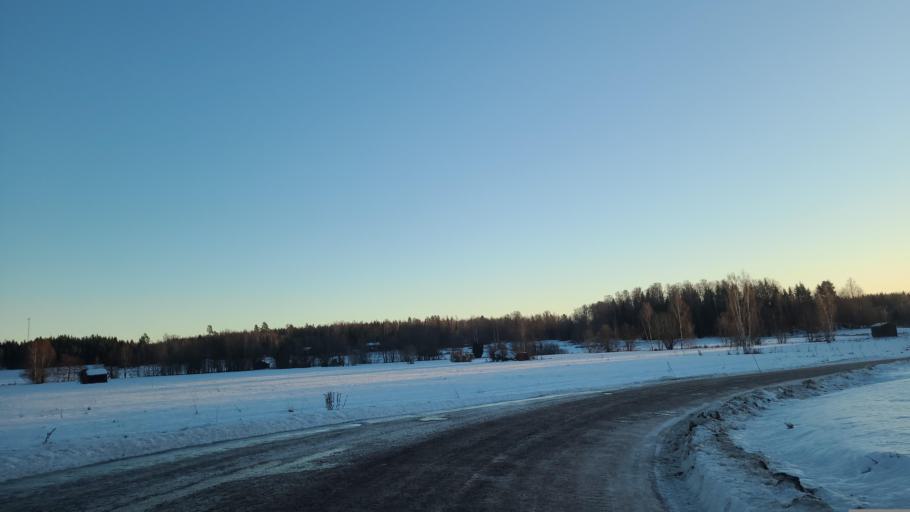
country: SE
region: Gaevleborg
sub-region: Soderhamns Kommun
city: Soderhamn
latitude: 61.2719
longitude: 16.9964
